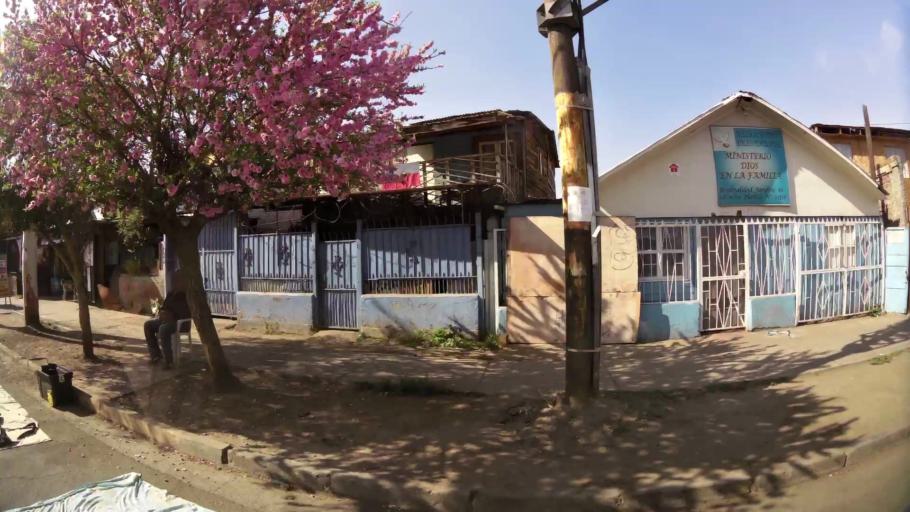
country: CL
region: Santiago Metropolitan
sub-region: Provincia de Santiago
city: Lo Prado
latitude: -33.4173
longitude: -70.7340
